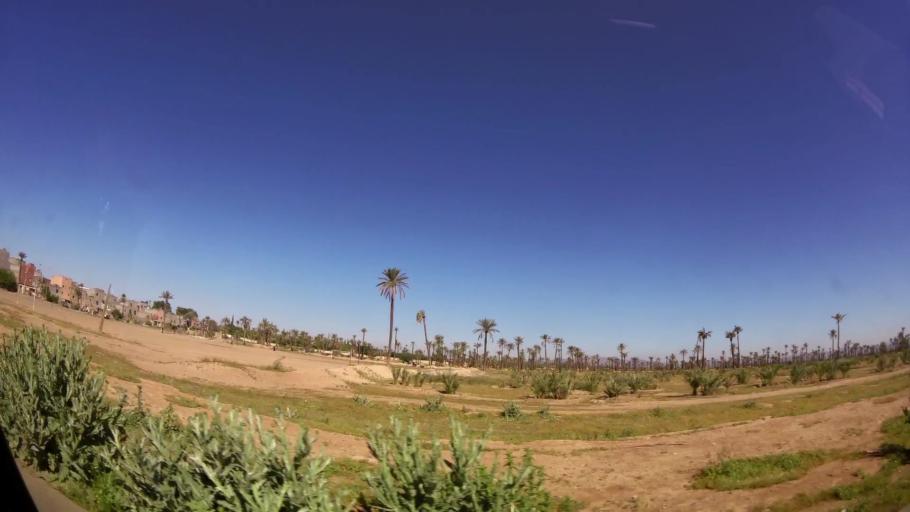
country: MA
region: Marrakech-Tensift-Al Haouz
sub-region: Marrakech
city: Marrakesh
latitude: 31.6570
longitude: -7.9515
